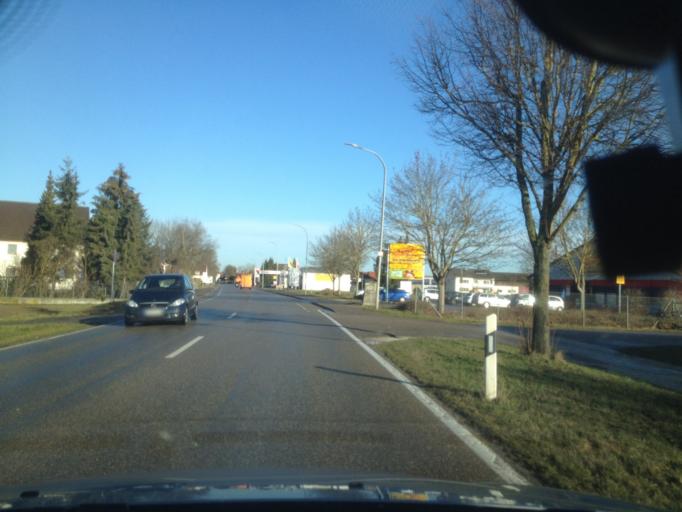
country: DE
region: Bavaria
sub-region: Swabia
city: Gundelfingen
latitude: 48.5422
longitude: 10.3669
